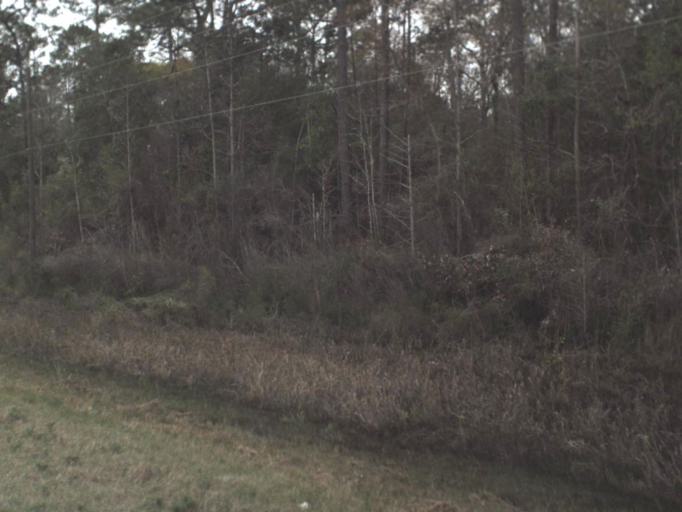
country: US
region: Florida
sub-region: Liberty County
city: Bristol
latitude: 30.2355
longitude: -84.8762
